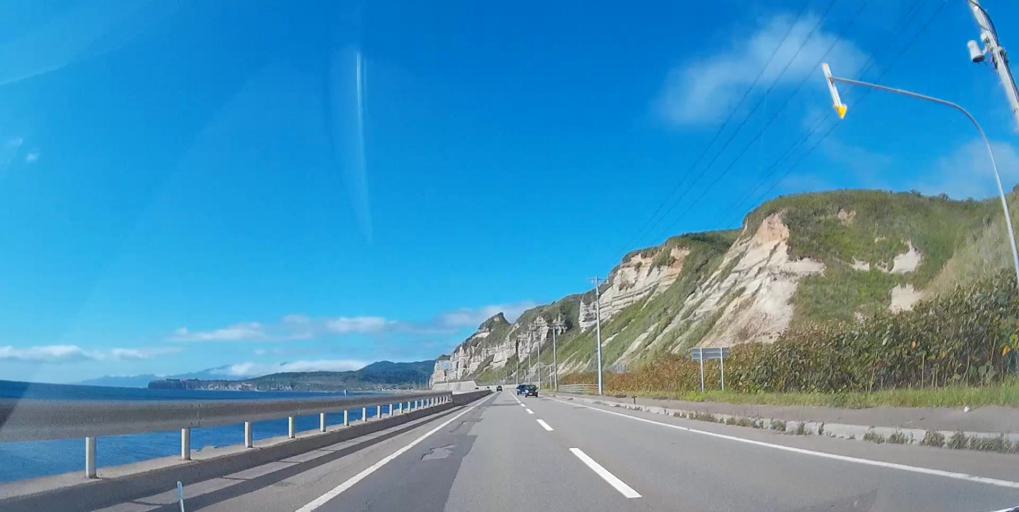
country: JP
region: Hokkaido
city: Kamiiso
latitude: 41.9845
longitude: 140.1259
